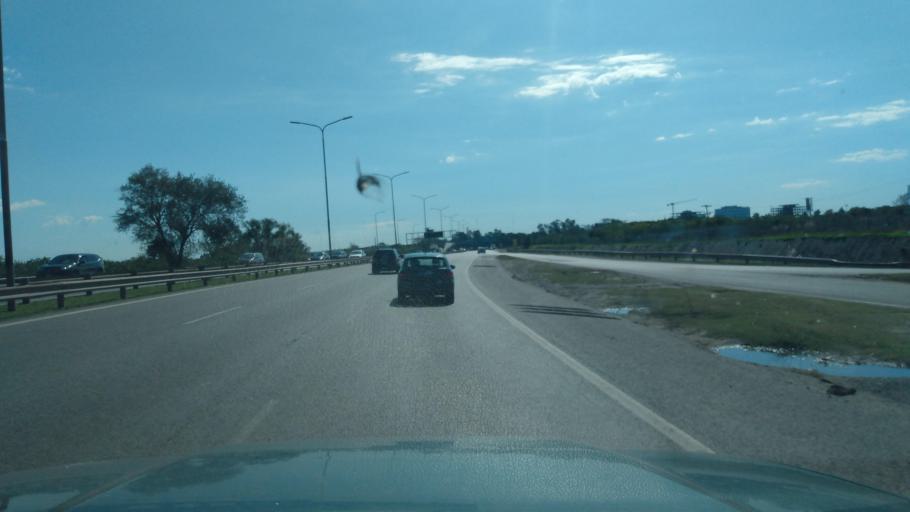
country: AR
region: Buenos Aires
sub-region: Partido de Tigre
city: Tigre
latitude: -34.4945
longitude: -58.5950
